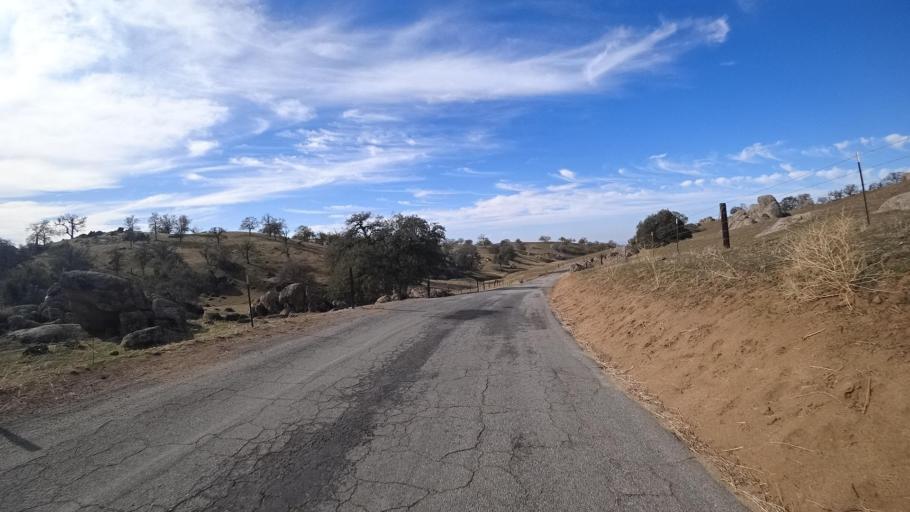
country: US
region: California
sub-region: Kern County
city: Oildale
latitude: 35.6148
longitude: -118.8439
